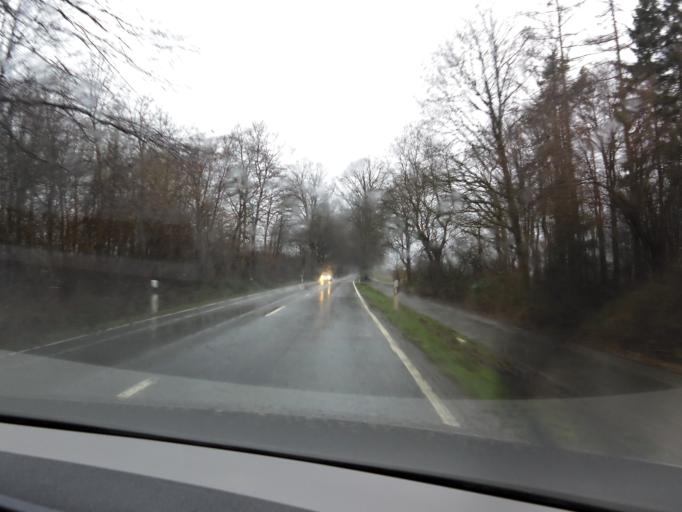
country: DE
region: Schleswig-Holstein
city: Mustin
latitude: 53.6934
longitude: 10.8548
